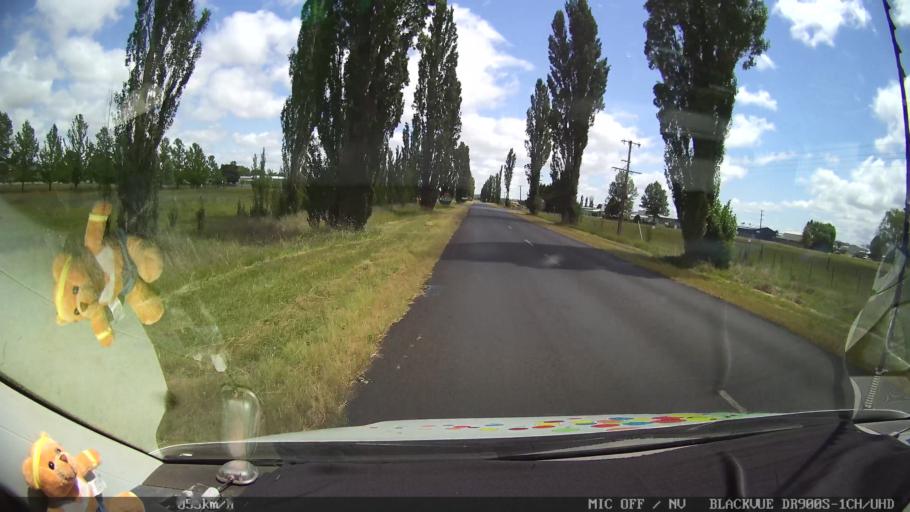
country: AU
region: New South Wales
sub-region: Glen Innes Severn
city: Glen Innes
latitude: -29.7258
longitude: 151.7257
